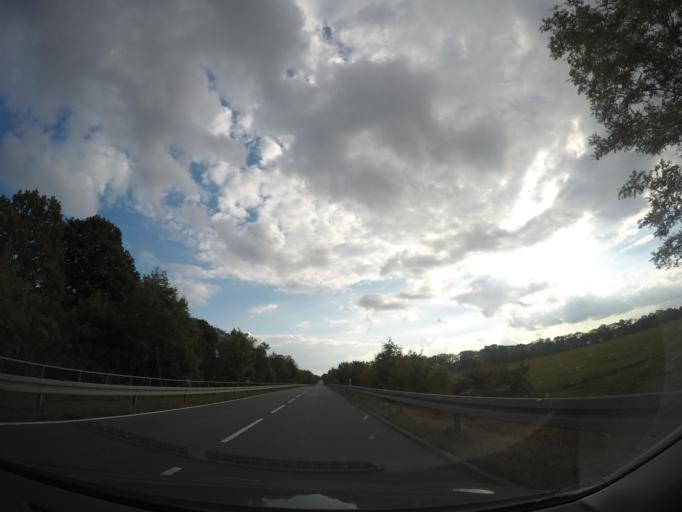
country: DE
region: Saxony-Anhalt
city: Mieste
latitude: 52.4299
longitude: 11.1366
